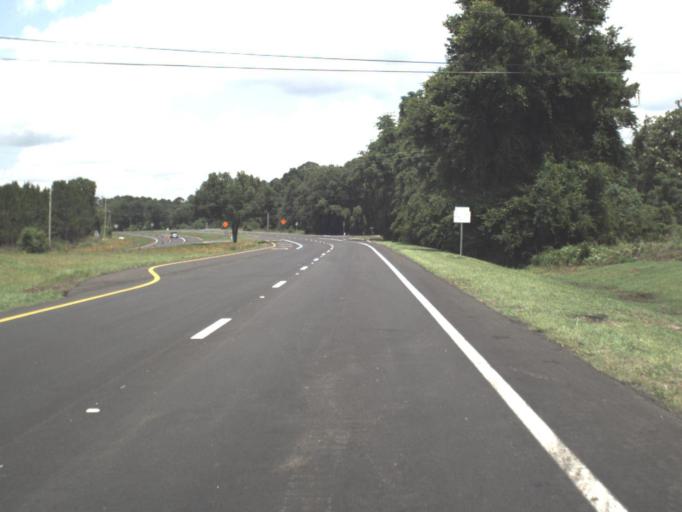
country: US
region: Florida
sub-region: Alachua County
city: Alachua
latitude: 29.7834
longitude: -82.4604
